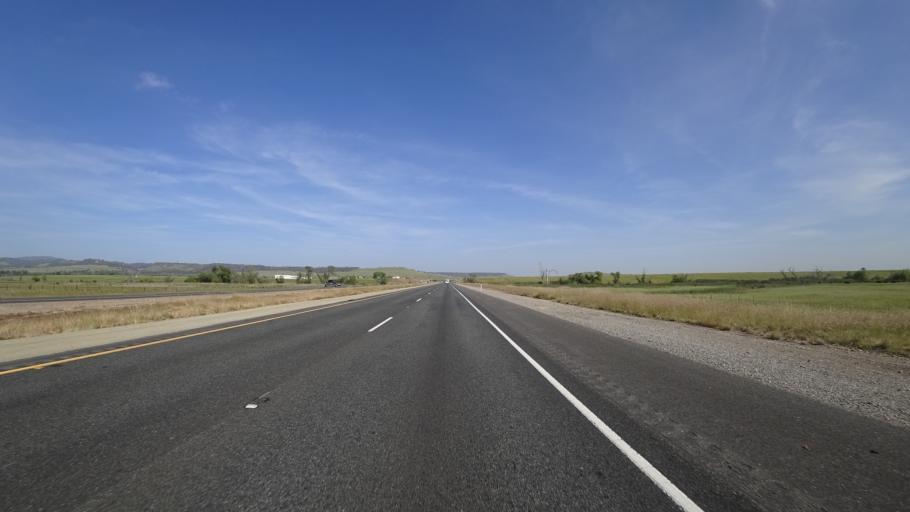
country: US
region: California
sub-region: Butte County
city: Thermalito
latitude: 39.5928
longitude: -121.6440
